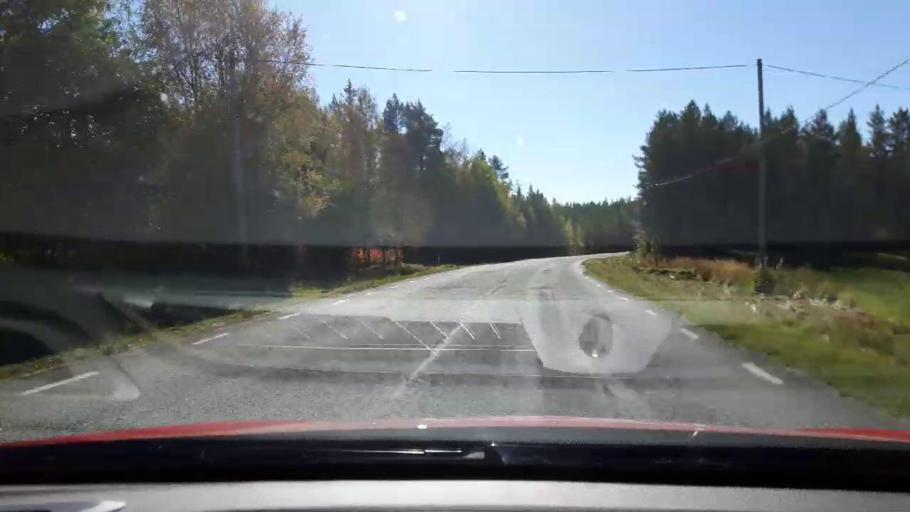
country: SE
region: Jaemtland
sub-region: Harjedalens Kommun
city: Sveg
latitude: 62.3260
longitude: 14.0611
